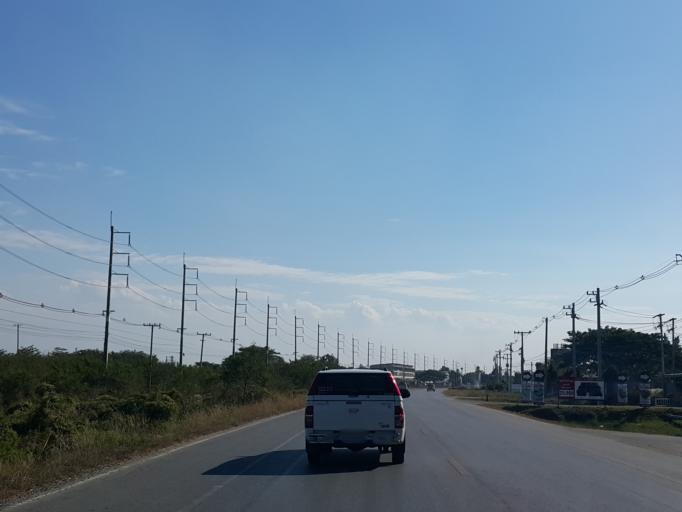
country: TH
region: Chiang Mai
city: San Kamphaeng
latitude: 18.7839
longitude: 99.0699
